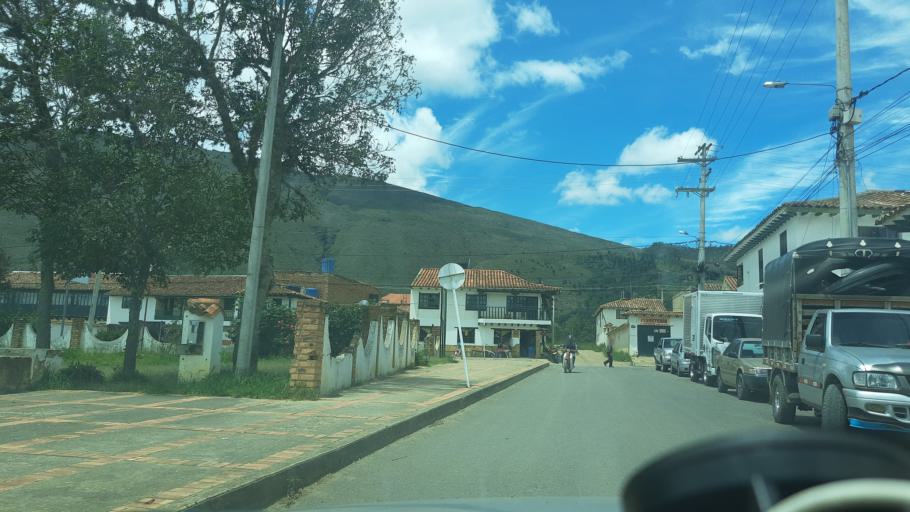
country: CO
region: Boyaca
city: Villa de Leiva
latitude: 5.6287
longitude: -73.5287
